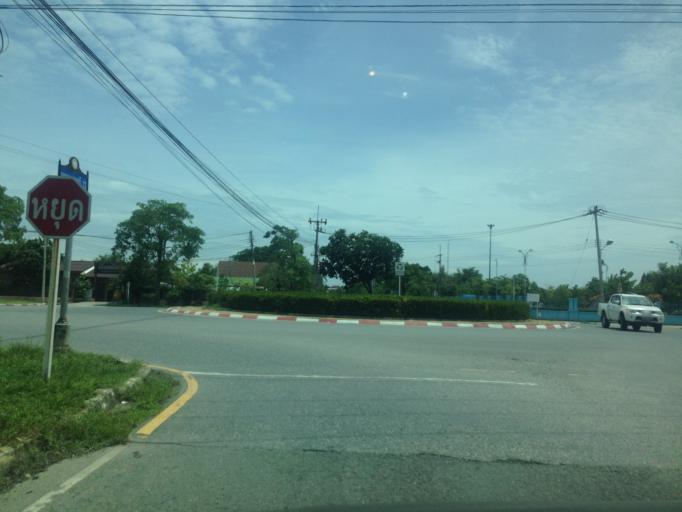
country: TH
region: Chon Buri
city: Chon Buri
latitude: 13.3432
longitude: 100.9502
